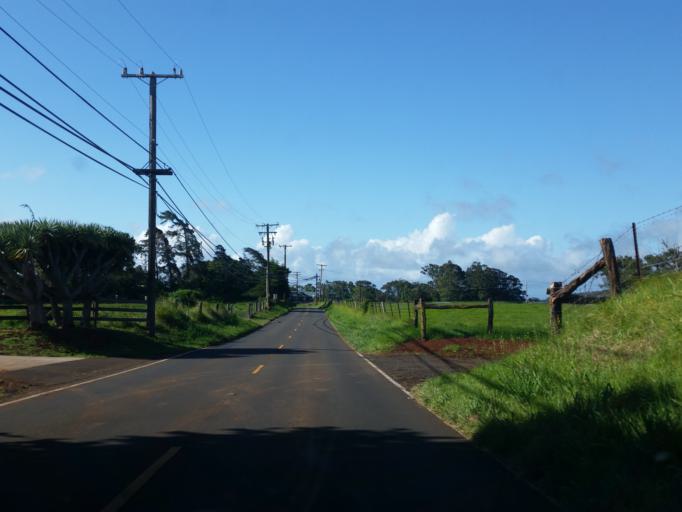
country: US
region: Hawaii
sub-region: Maui County
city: Makawao
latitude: 20.8476
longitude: -156.3085
